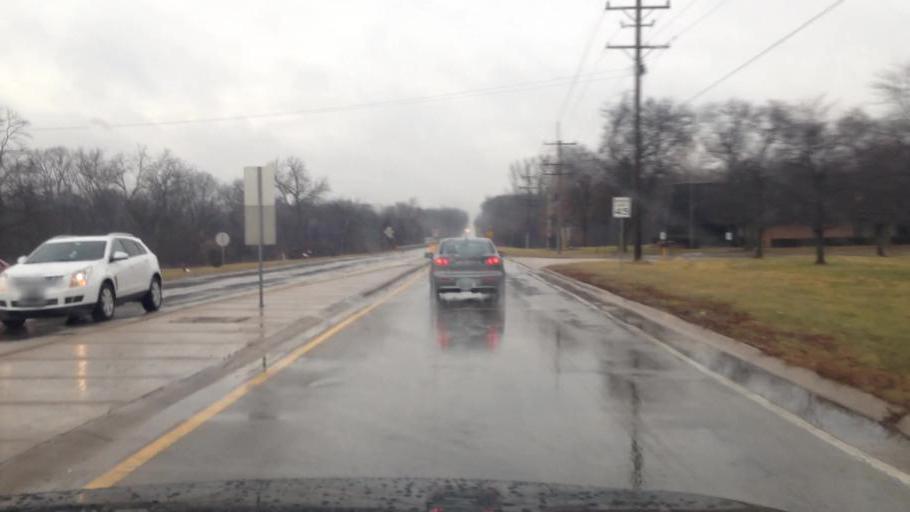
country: US
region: Illinois
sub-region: Will County
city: Ingalls Park
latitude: 41.5241
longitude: -88.0048
